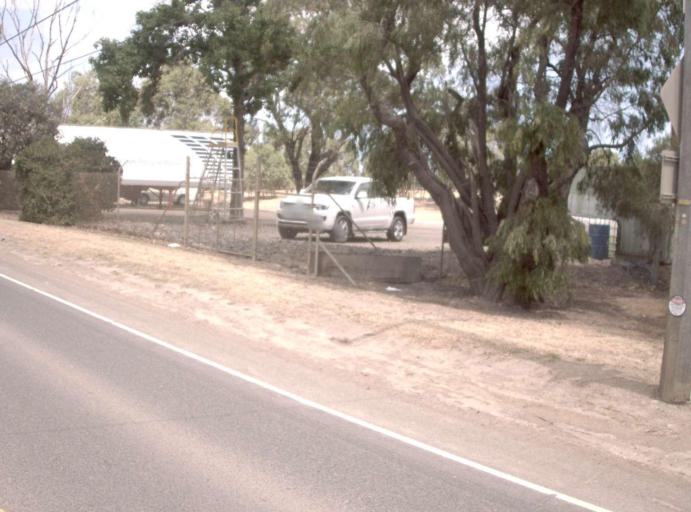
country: AU
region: Victoria
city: Heatherton
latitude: -37.9502
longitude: 145.0981
